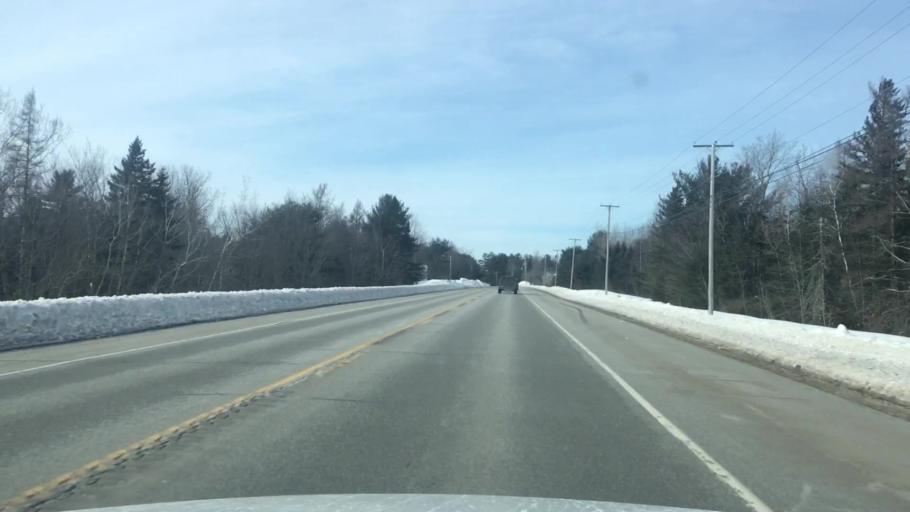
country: US
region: Maine
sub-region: Penobscot County
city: Kenduskeag
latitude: 44.9552
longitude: -68.9511
